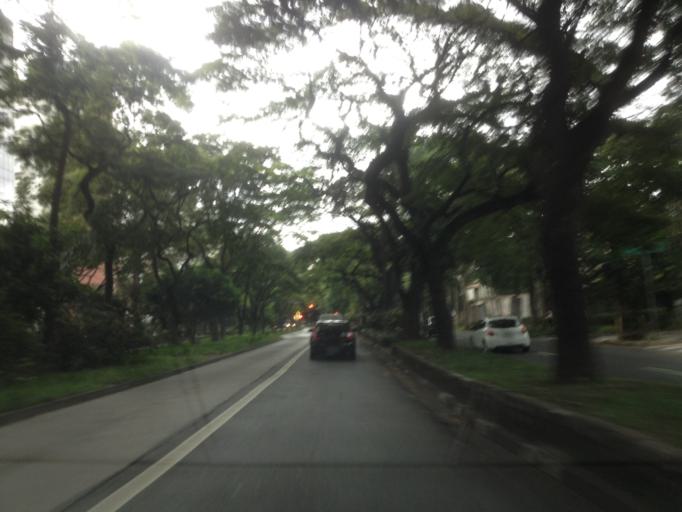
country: BR
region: Sao Paulo
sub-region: Sao Paulo
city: Sao Paulo
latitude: -23.5775
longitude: -46.6739
